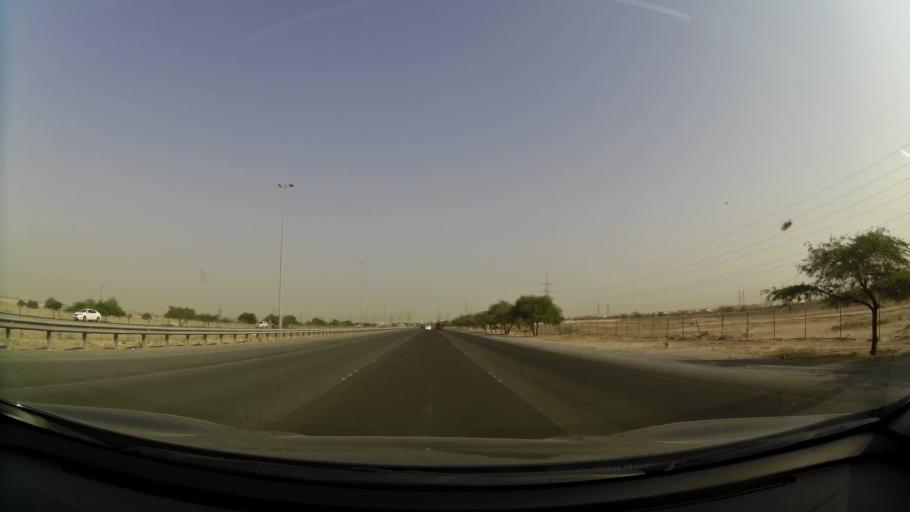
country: KW
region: Al Asimah
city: Ar Rabiyah
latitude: 29.2221
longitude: 47.8853
